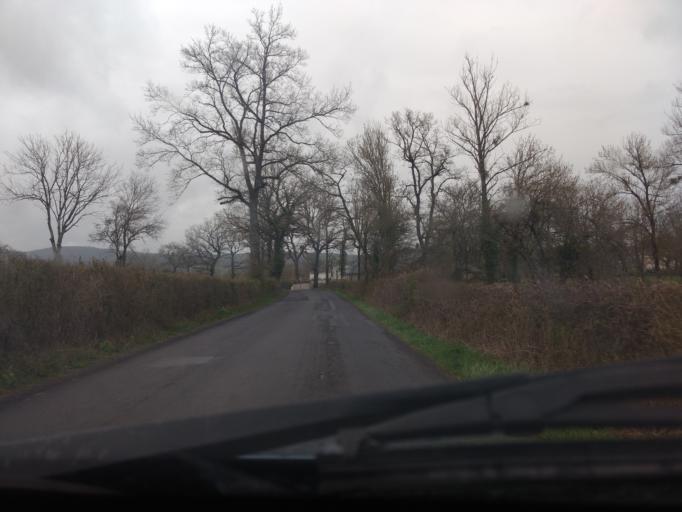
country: FR
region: Midi-Pyrenees
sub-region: Departement de l'Aveyron
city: La Loubiere
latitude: 44.3950
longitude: 2.6891
